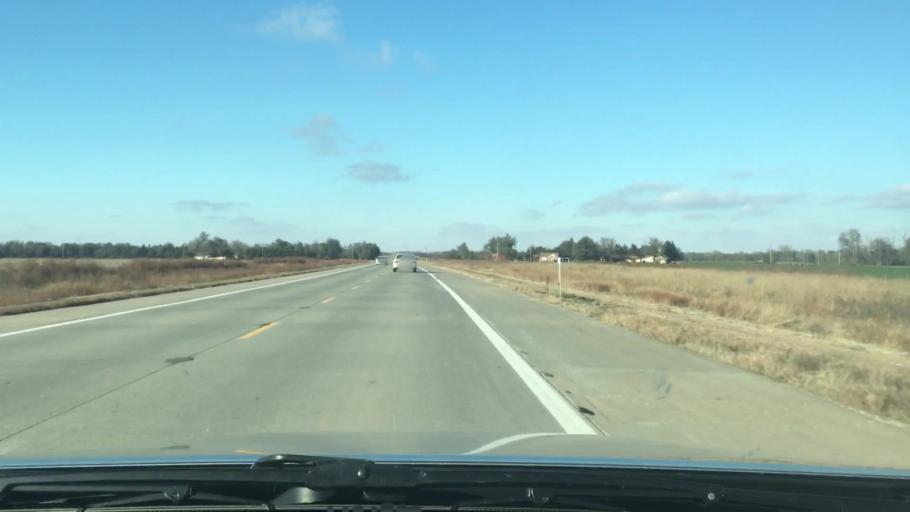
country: US
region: Kansas
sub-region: Reno County
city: Hutchinson
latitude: 38.0673
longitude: -97.9864
